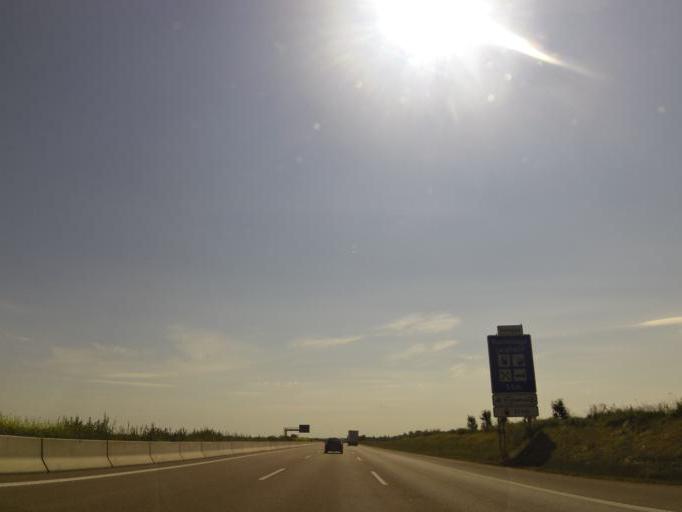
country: DE
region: Bavaria
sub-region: Swabia
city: Nersingen
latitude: 48.4615
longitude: 10.1496
